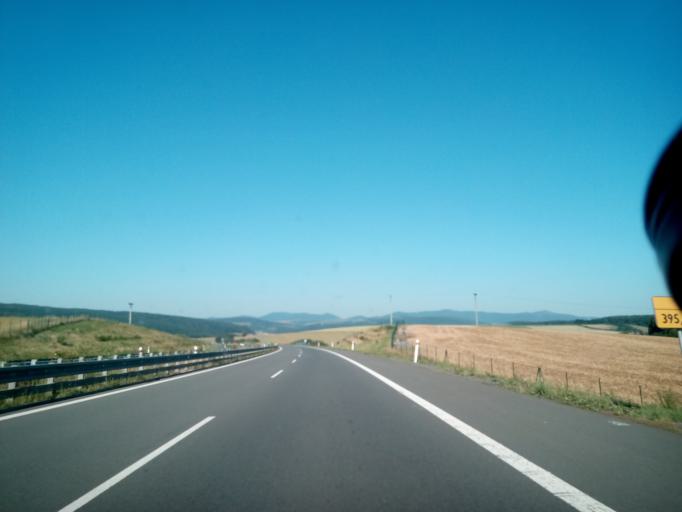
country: SK
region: Presovsky
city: Sabinov
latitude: 49.0078
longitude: 21.1316
